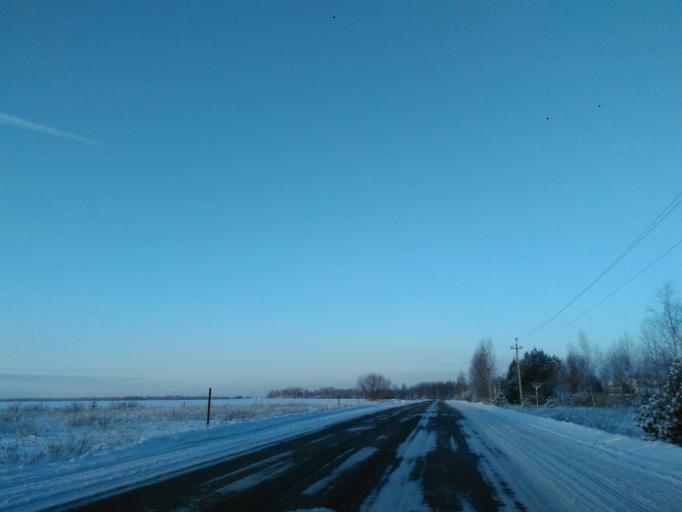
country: RU
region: Tverskaya
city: Zavidovo
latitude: 56.6078
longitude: 36.6093
